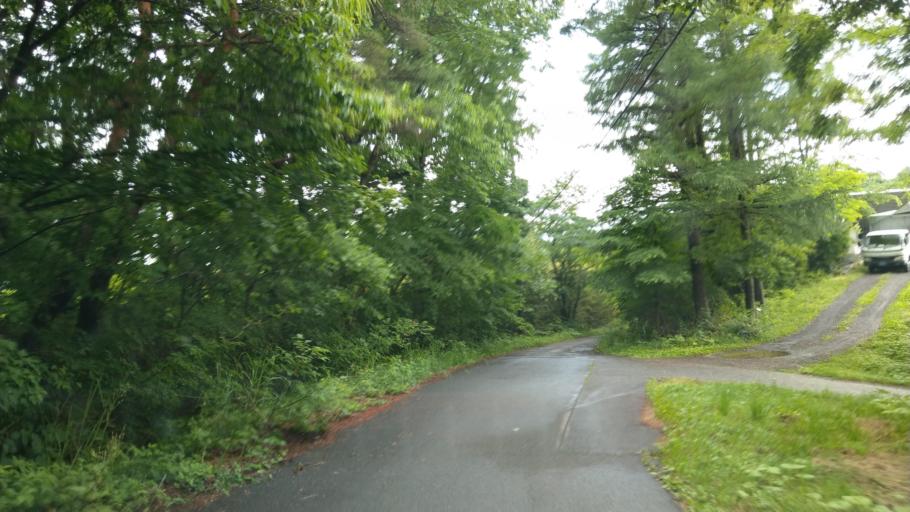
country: JP
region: Nagano
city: Komoro
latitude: 36.2759
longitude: 138.3717
